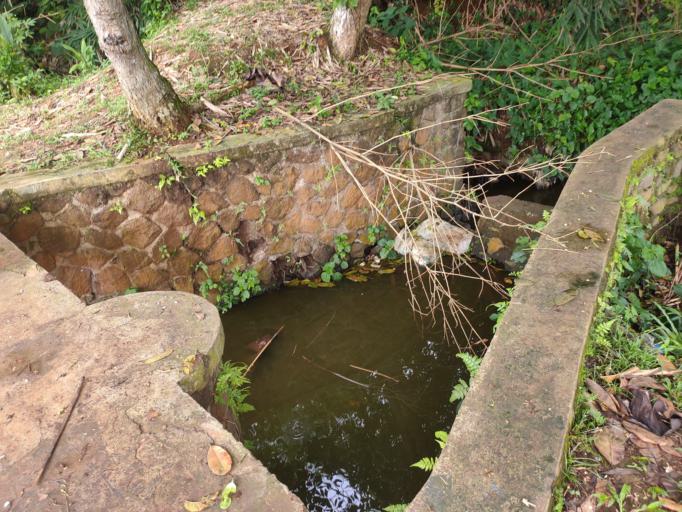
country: ID
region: West Java
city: Ciampea
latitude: -6.5242
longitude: 106.7029
